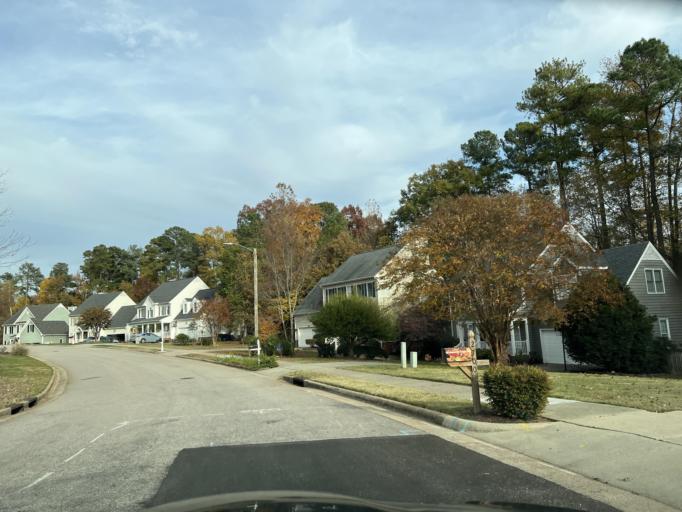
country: US
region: North Carolina
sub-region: Wake County
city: Wake Forest
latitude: 35.9013
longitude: -78.5919
